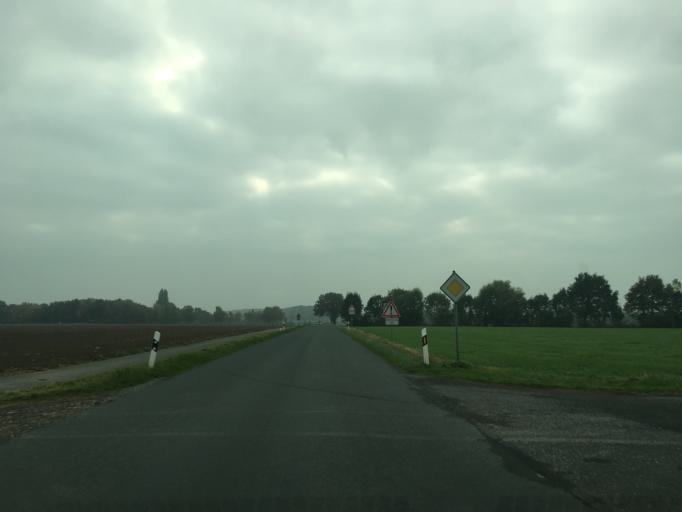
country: DE
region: North Rhine-Westphalia
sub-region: Regierungsbezirk Munster
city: Laer
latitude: 52.0270
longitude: 7.3762
